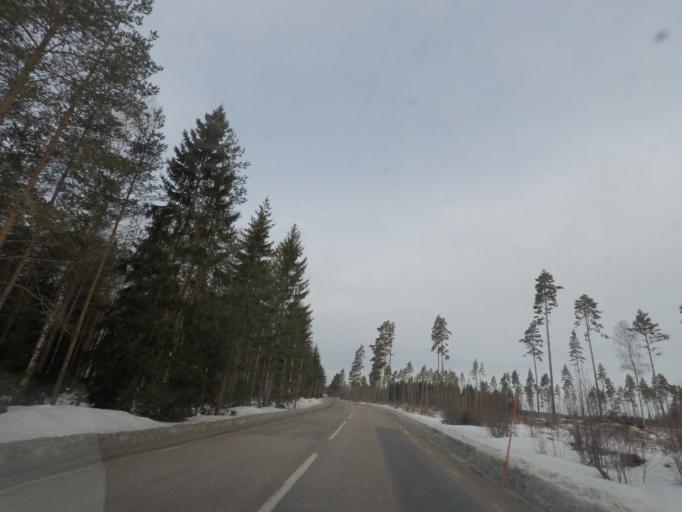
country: SE
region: Vaestmanland
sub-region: Vasteras
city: Skultuna
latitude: 59.7537
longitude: 16.3178
